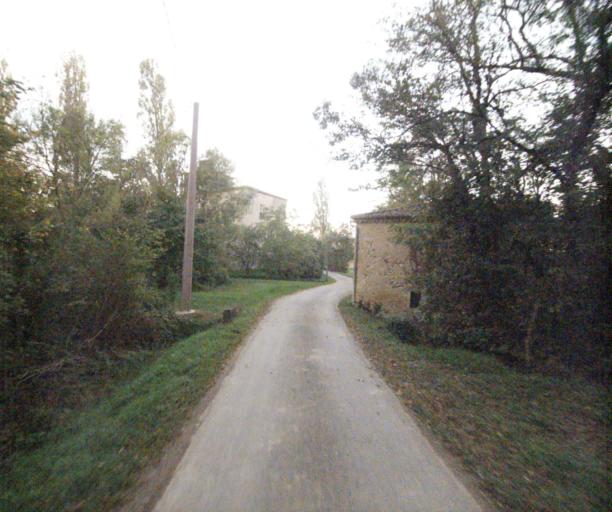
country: FR
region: Midi-Pyrenees
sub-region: Departement du Gers
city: Vic-Fezensac
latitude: 43.8086
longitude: 0.2573
